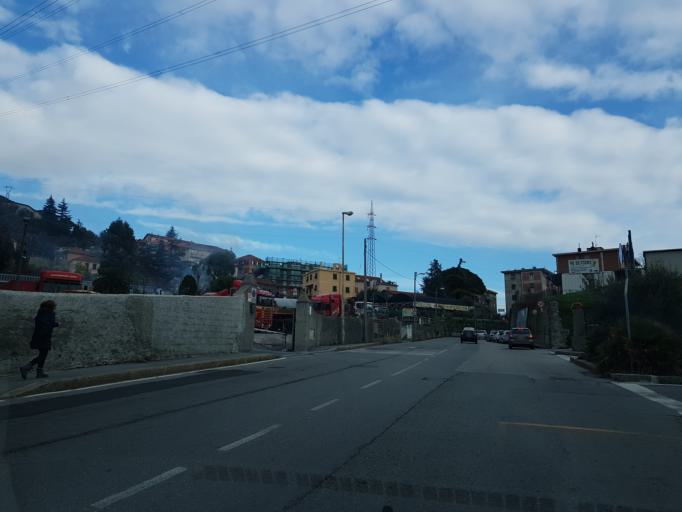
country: IT
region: Liguria
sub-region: Provincia di Genova
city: San Teodoro
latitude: 44.4365
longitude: 8.8732
